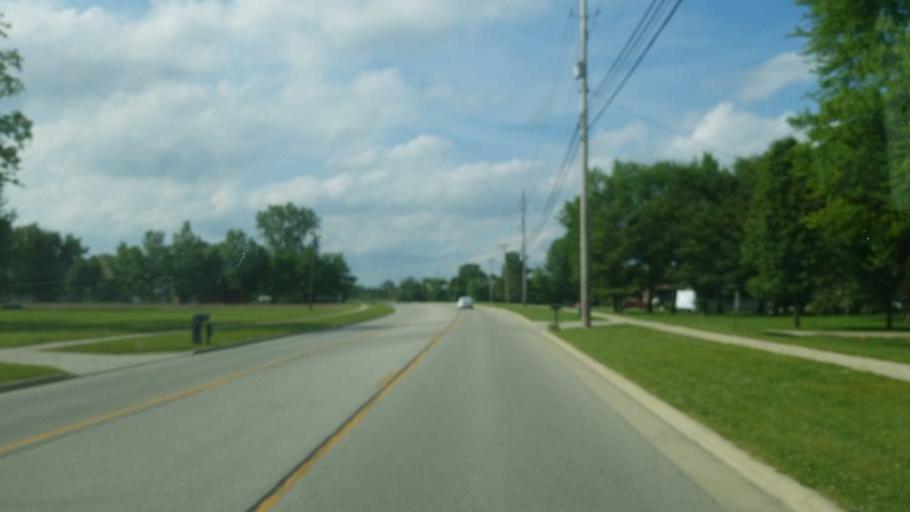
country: US
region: Ohio
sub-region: Franklin County
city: Westerville
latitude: 40.1670
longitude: -82.8995
